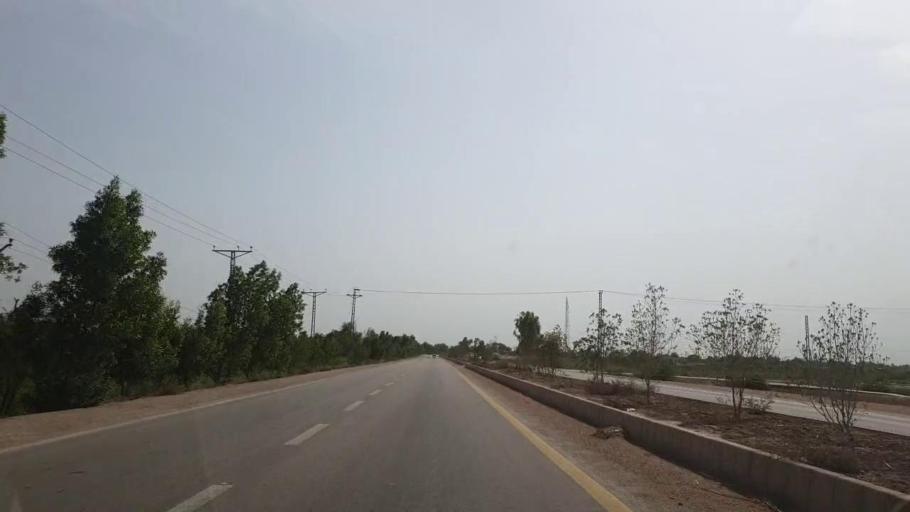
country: PK
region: Sindh
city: Sakrand
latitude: 26.2011
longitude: 68.3128
